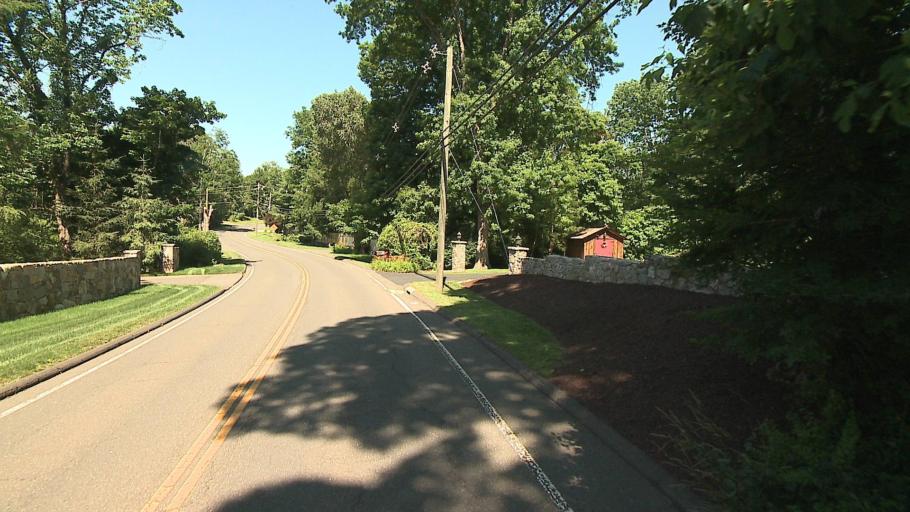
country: US
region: Connecticut
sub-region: Fairfield County
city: Ridgefield
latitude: 41.2825
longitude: -73.5107
